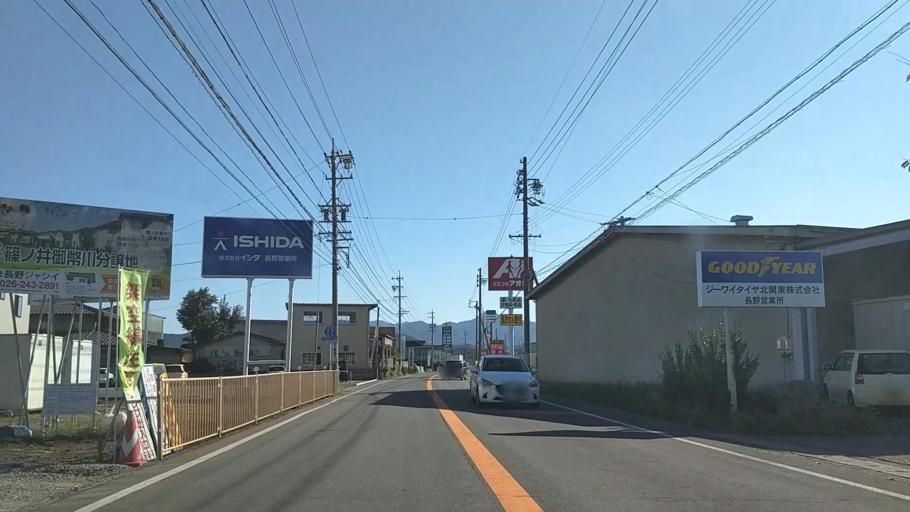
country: JP
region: Nagano
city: Nagano-shi
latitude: 36.5686
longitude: 138.1414
